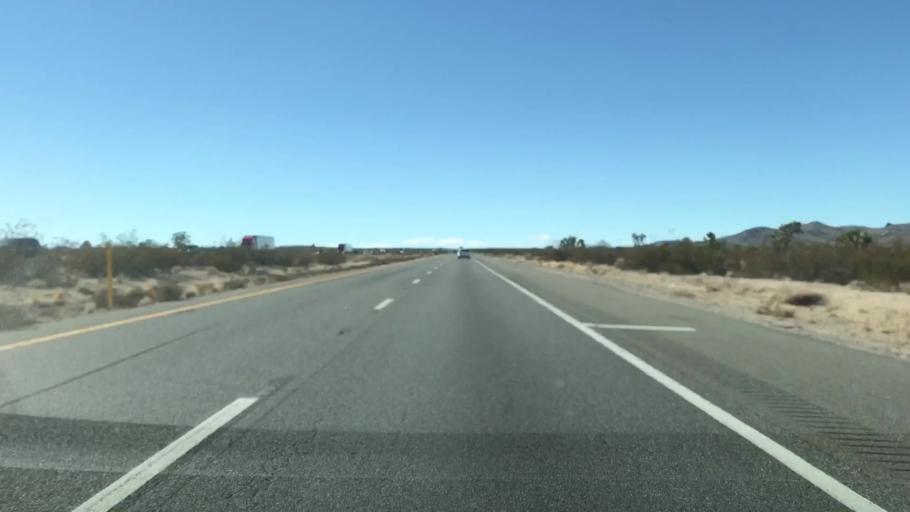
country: US
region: Nevada
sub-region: Clark County
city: Sandy Valley
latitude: 35.4168
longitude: -115.7522
